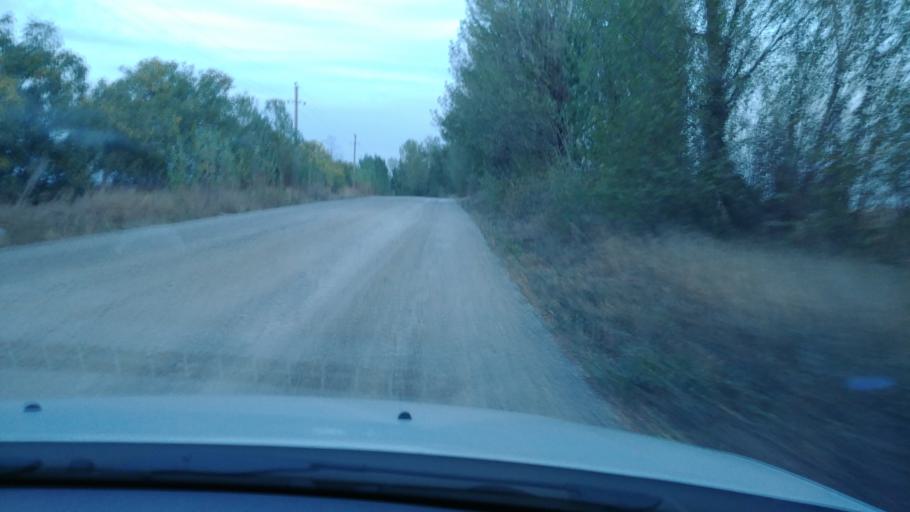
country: MD
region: Rezina
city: Saharna
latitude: 47.6803
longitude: 28.9173
